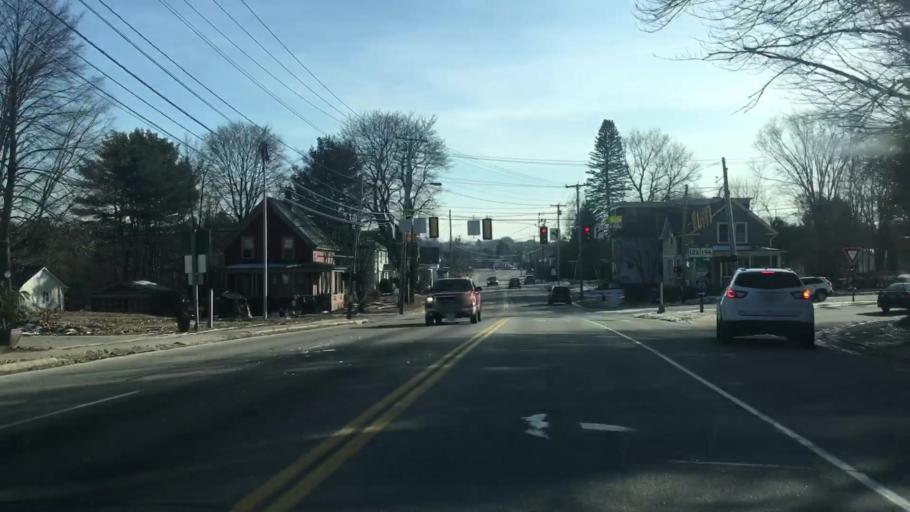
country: US
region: Maine
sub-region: Androscoggin County
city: Lewiston
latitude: 44.1036
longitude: -70.1926
